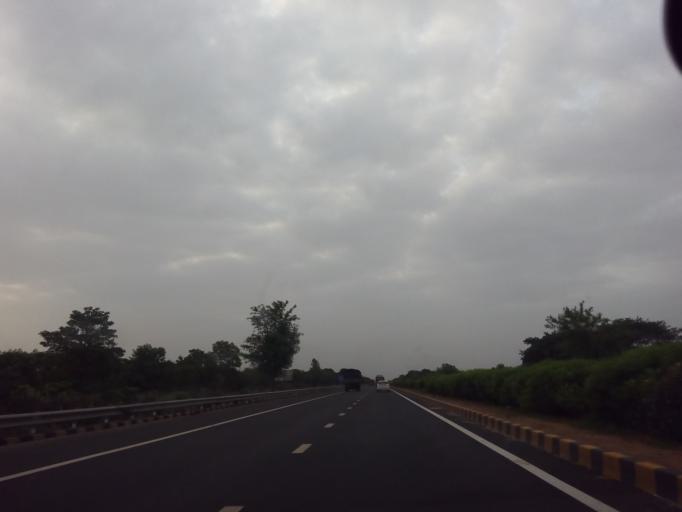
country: IN
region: Gujarat
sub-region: Kheda
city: Mahemdavad
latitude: 22.9276
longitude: 72.7388
